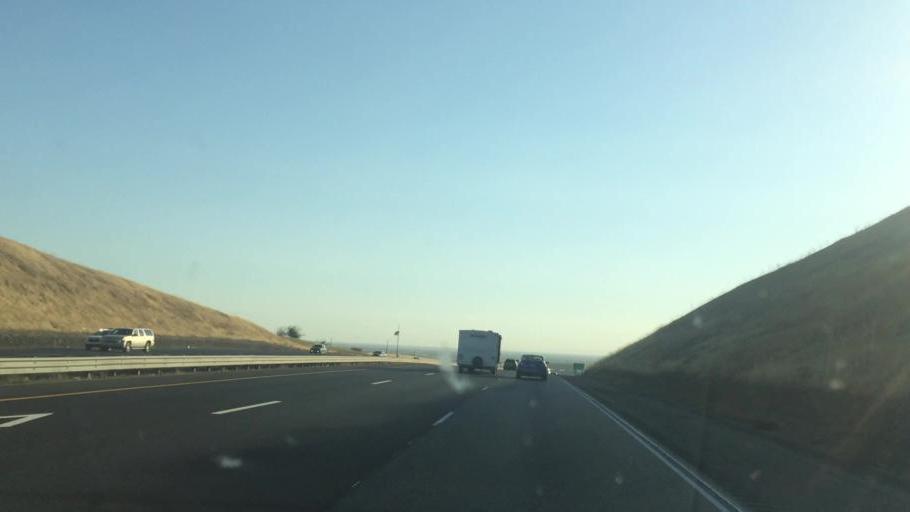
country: US
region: California
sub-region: El Dorado County
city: El Dorado Hills
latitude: 38.6451
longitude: -121.0945
